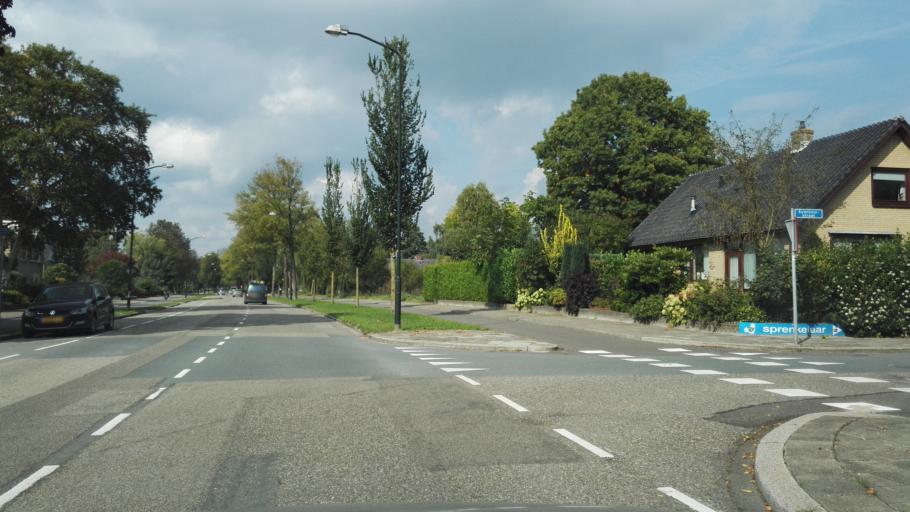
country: NL
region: Gelderland
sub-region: Gemeente Apeldoorn
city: Apeldoorn
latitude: 52.2293
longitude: 5.9940
